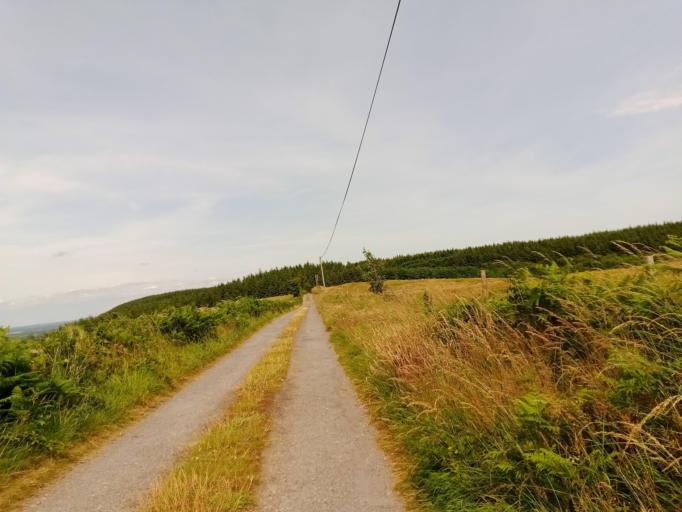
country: IE
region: Leinster
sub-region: Laois
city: Rathdowney
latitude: 52.7975
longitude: -7.4640
